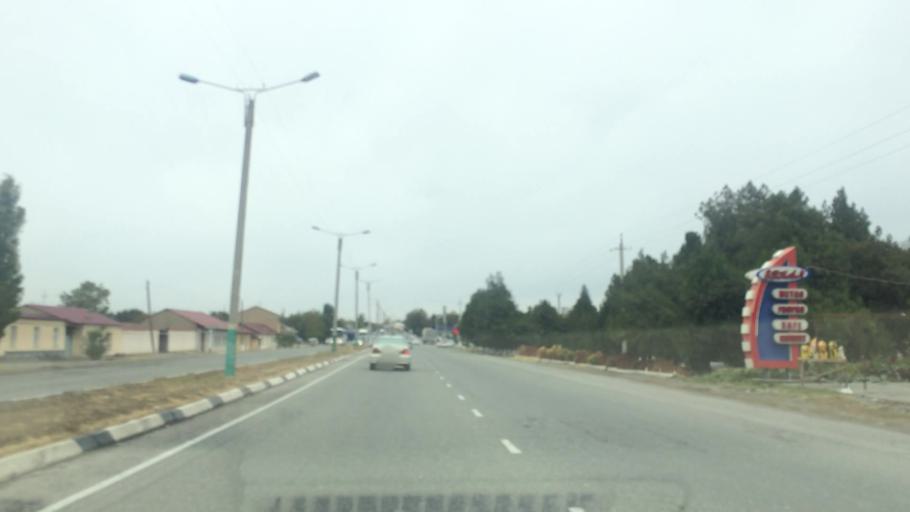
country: UZ
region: Samarqand
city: Bulung'ur
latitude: 39.7707
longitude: 67.2723
